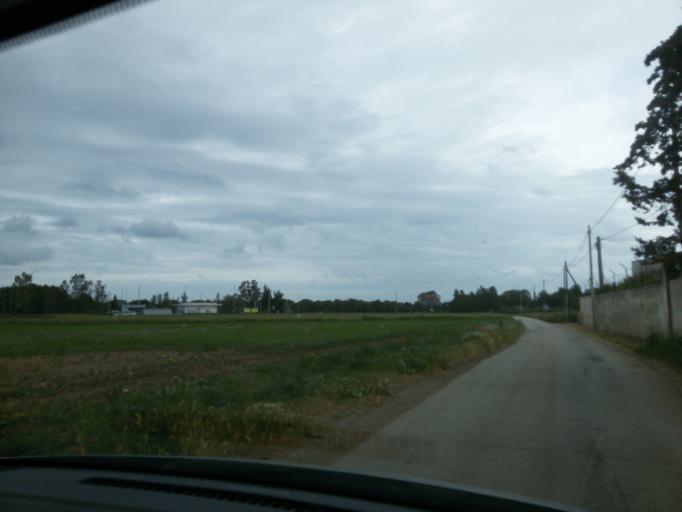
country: IT
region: Apulia
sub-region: Provincia di Brindisi
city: Brindisi
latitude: 40.6579
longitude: 17.9245
